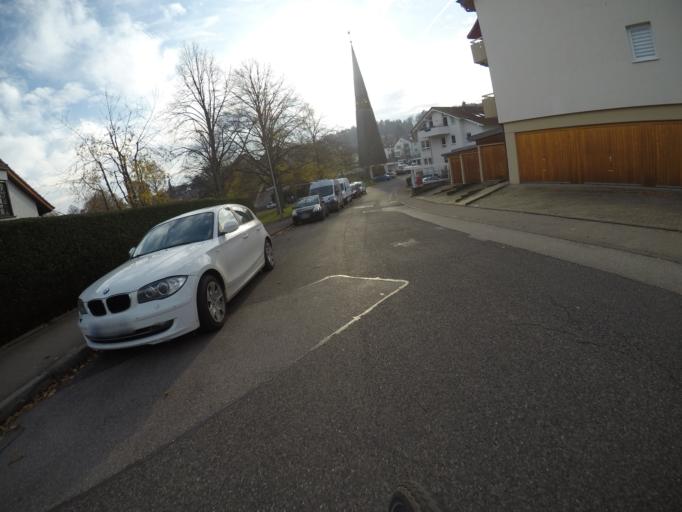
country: DE
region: Baden-Wuerttemberg
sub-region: Regierungsbezirk Stuttgart
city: Steinenbronn
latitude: 48.7049
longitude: 9.1187
